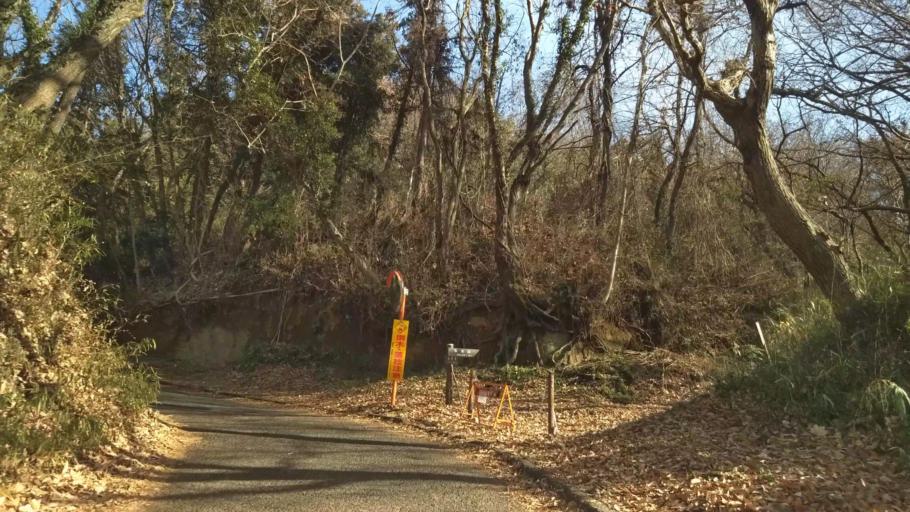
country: JP
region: Kanagawa
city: Hadano
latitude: 35.3731
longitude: 139.2393
